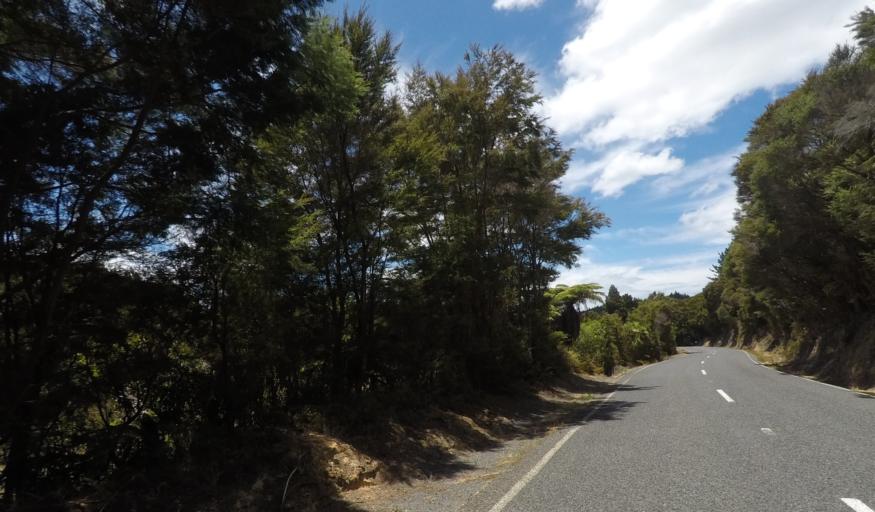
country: NZ
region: Northland
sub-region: Whangarei
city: Ngunguru
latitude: -35.5066
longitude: 174.4022
